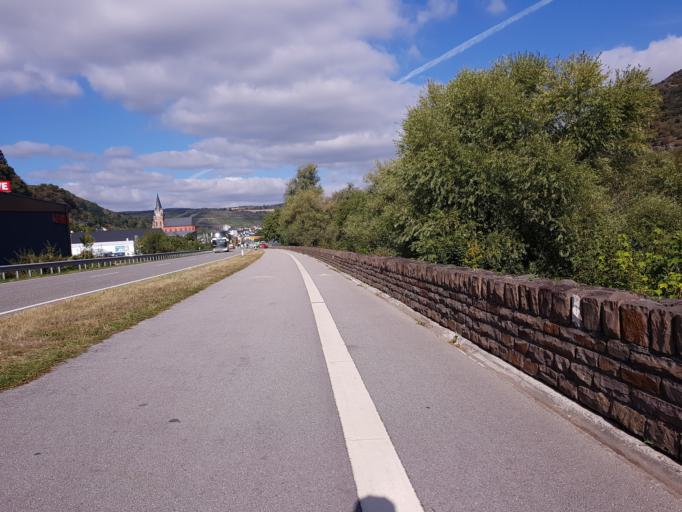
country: DE
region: Rheinland-Pfalz
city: Dorscheid
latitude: 50.1005
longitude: 7.7396
